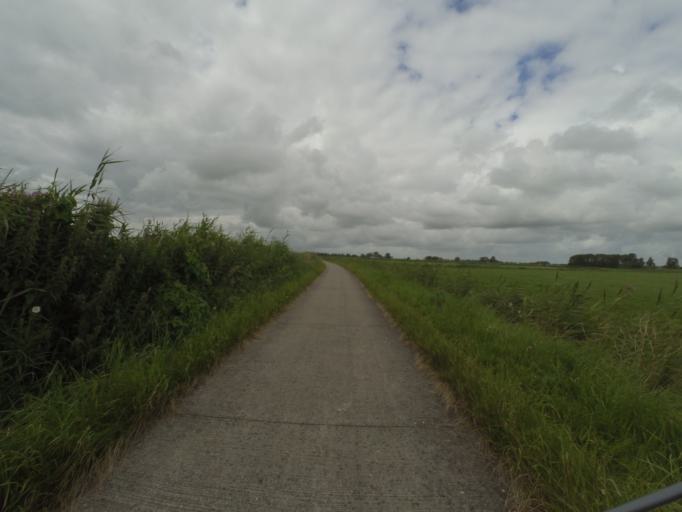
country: NL
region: Friesland
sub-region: Gemeente Kollumerland en Nieuwkruisland
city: Kollum
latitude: 53.3203
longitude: 6.1220
